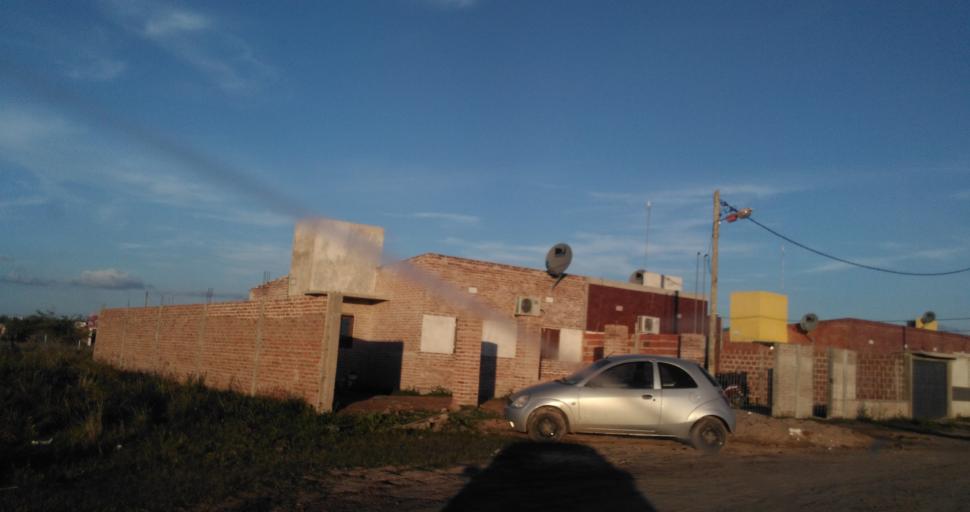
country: AR
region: Chaco
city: Resistencia
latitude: -27.4712
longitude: -59.0248
